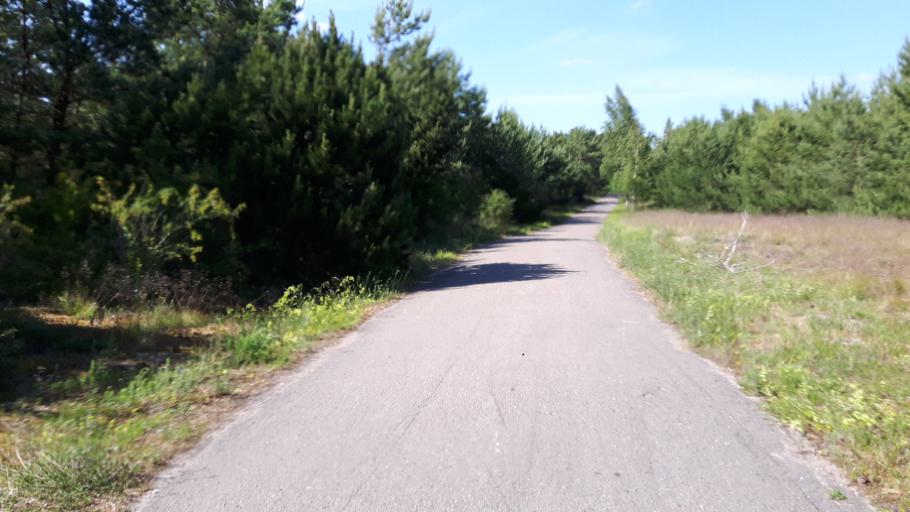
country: LT
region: Klaipedos apskritis
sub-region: Klaipeda
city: Klaipeda
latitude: 55.6912
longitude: 21.1029
